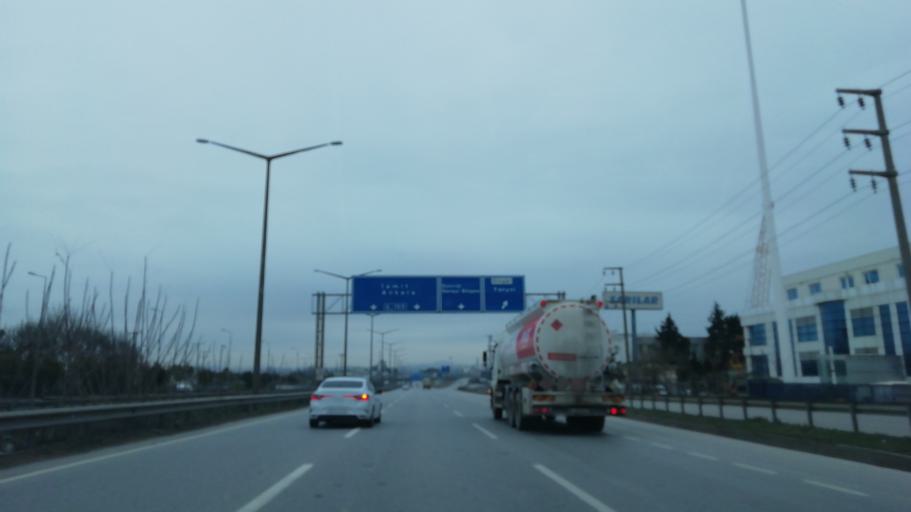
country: TR
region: Kocaeli
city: Gebze
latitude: 40.7996
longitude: 29.4550
